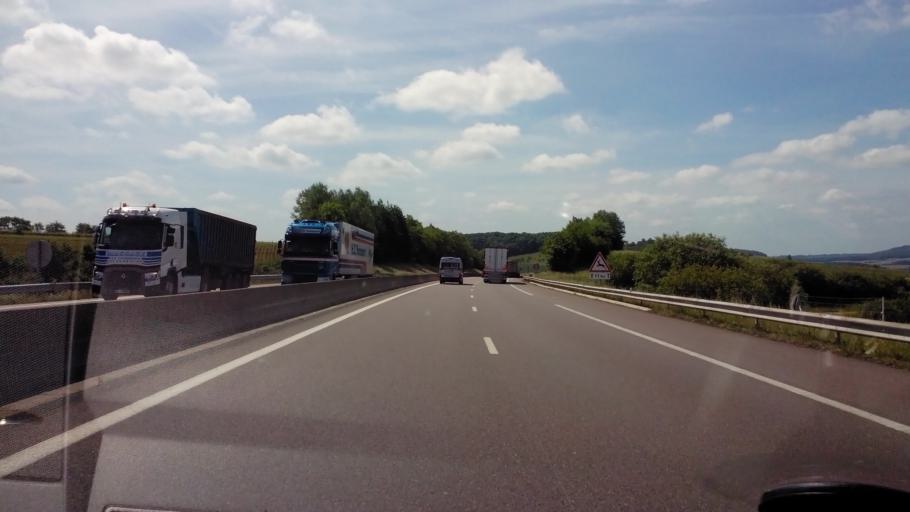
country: FR
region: Lorraine
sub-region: Departement des Vosges
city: Chatenois
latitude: 48.3813
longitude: 5.8822
